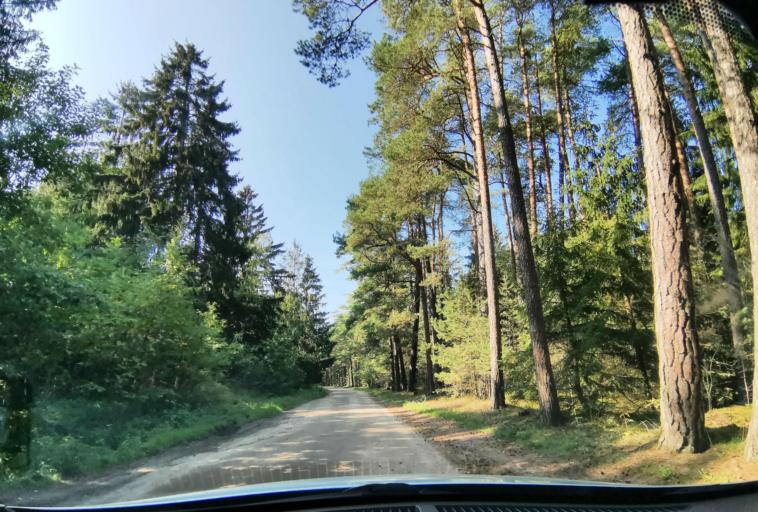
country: LT
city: Nida
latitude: 55.1604
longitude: 20.8341
